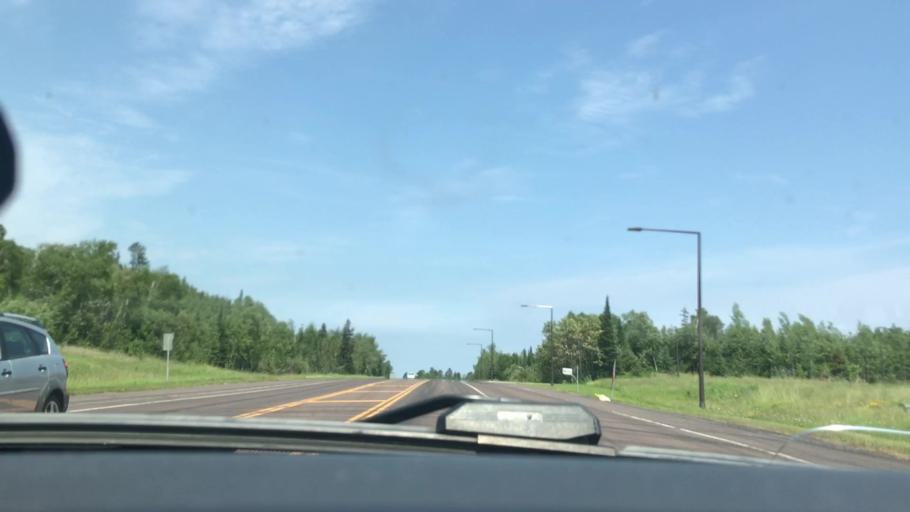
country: US
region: Minnesota
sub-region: Lake County
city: Silver Bay
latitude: 47.3391
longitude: -91.1977
